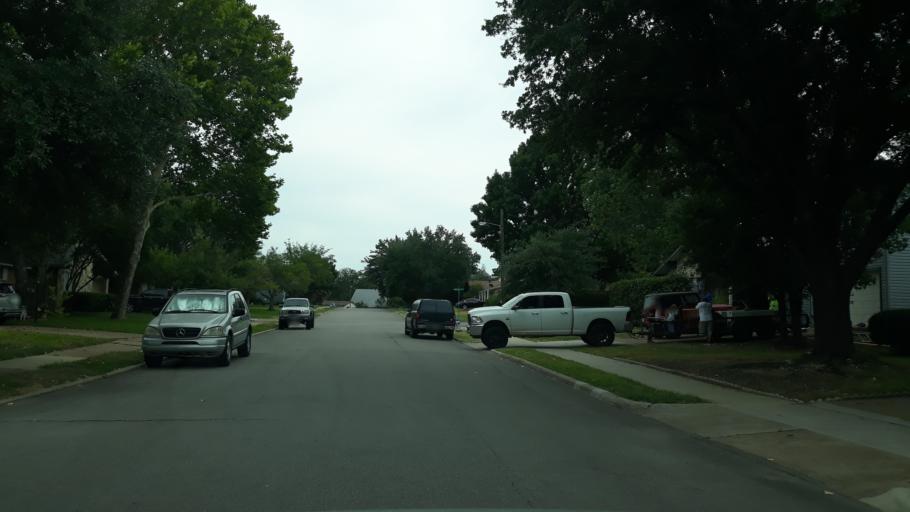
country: US
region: Texas
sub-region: Dallas County
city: Irving
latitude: 32.8434
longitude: -96.9869
